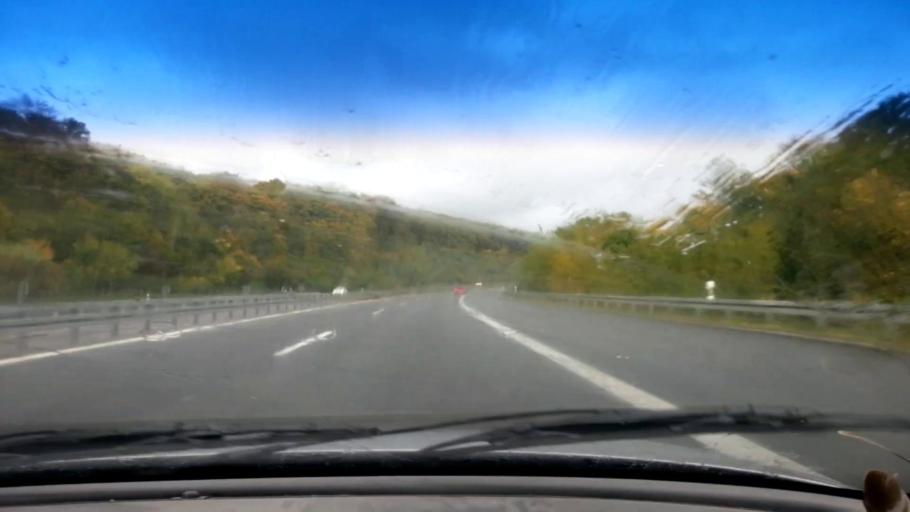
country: DE
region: Bavaria
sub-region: Upper Franconia
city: Schesslitz
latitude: 49.9839
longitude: 11.0736
